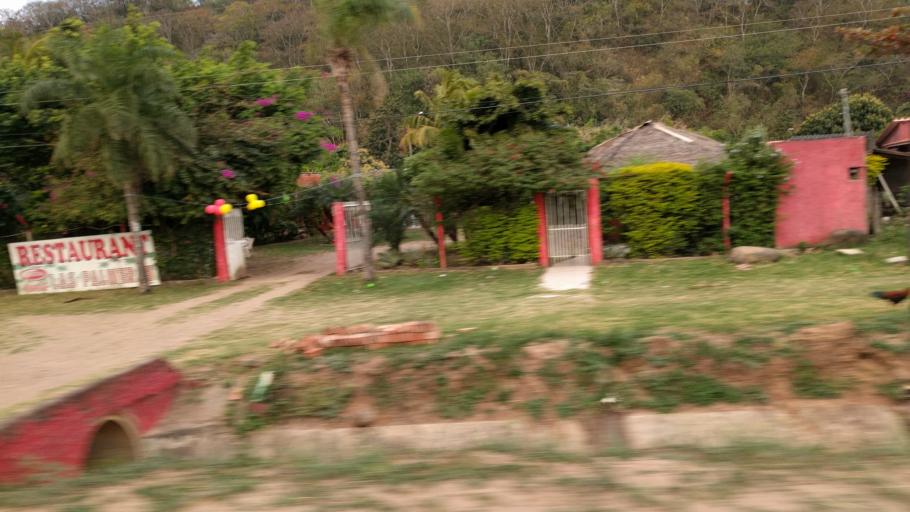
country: BO
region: Santa Cruz
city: Jorochito
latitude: -18.0873
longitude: -63.4505
